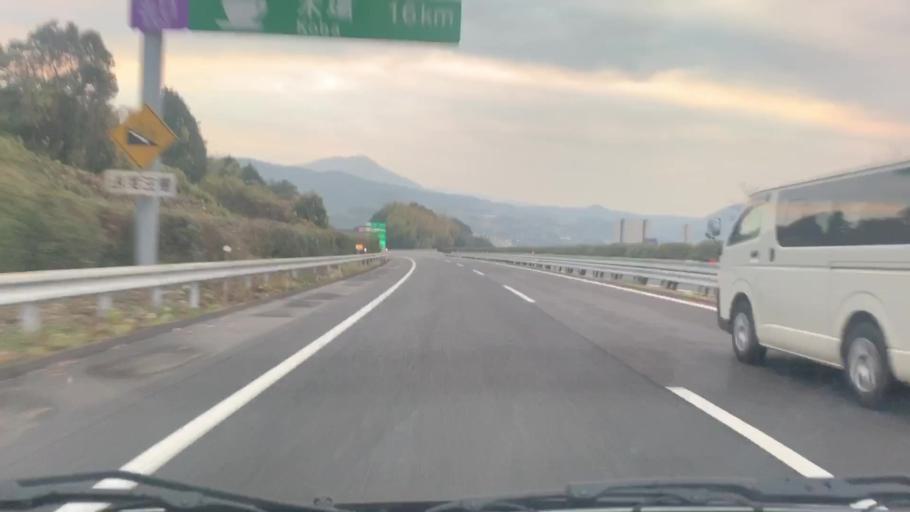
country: JP
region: Nagasaki
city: Omura
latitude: 33.0292
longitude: 129.9314
